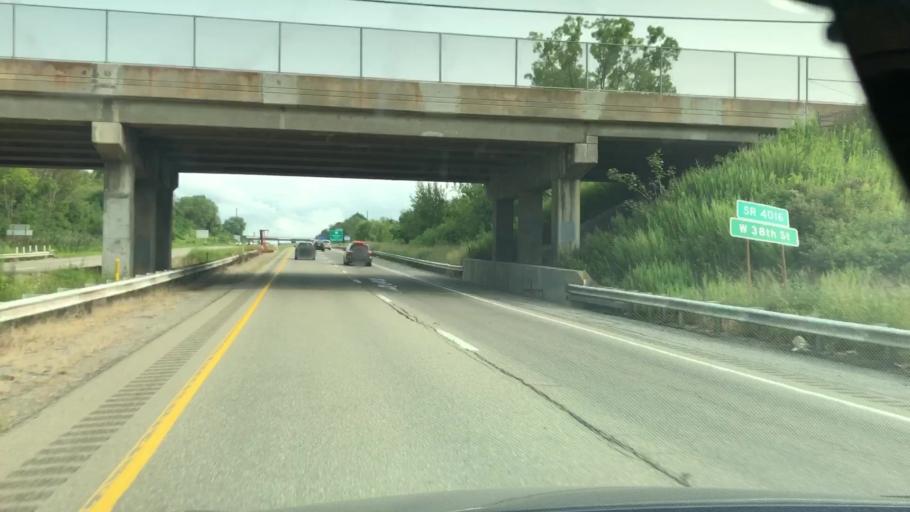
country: US
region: Pennsylvania
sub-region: Erie County
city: Erie
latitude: 42.0844
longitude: -80.1155
